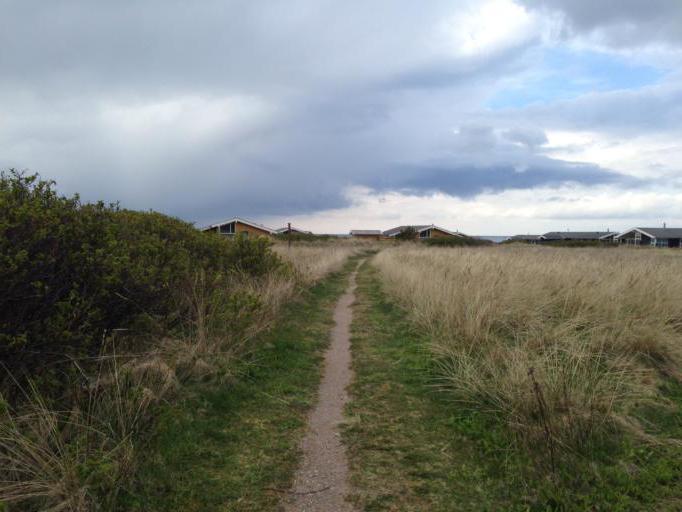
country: DK
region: North Denmark
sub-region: Hjorring Kommune
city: Hjorring
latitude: 57.4914
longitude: 9.8332
